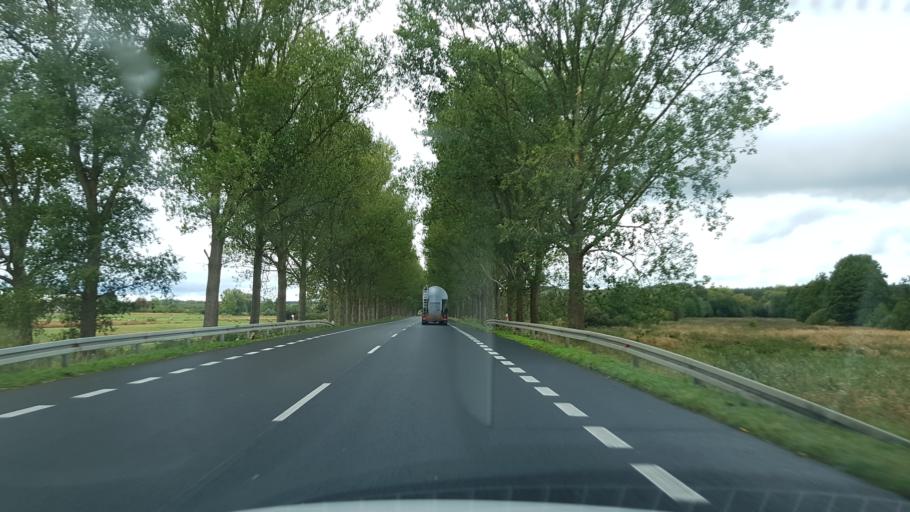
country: PL
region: West Pomeranian Voivodeship
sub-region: Powiat kamienski
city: Wolin
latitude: 53.8519
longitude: 14.5928
